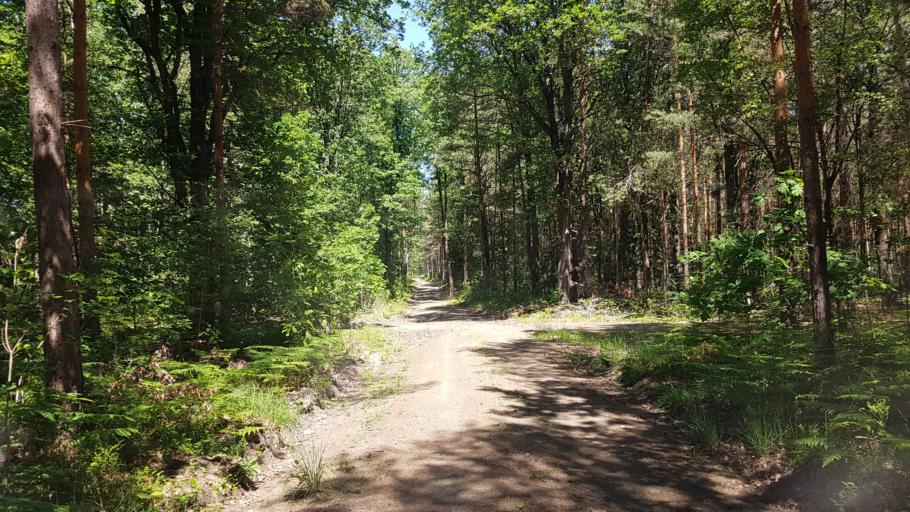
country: DE
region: Brandenburg
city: Hohenleipisch
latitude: 51.5320
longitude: 13.5774
